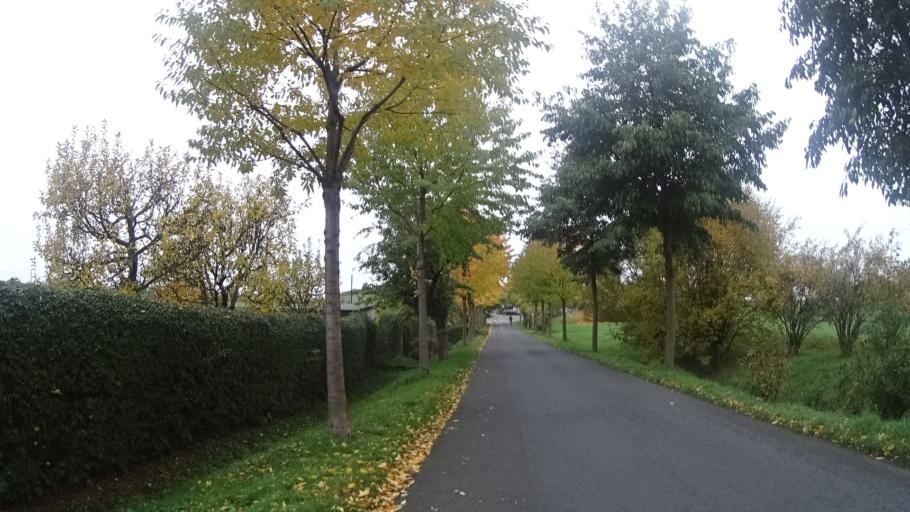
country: DE
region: Thuringia
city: Arnstadt
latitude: 50.8455
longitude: 10.9310
